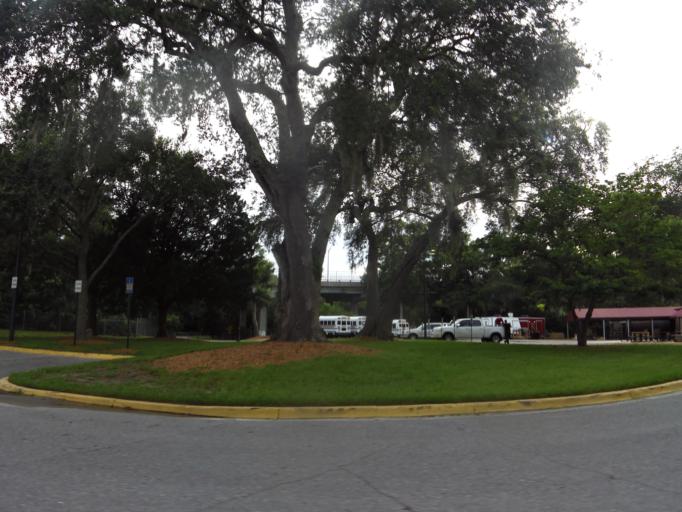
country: US
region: Florida
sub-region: Duval County
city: Jacksonville
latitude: 30.3104
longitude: -81.6226
